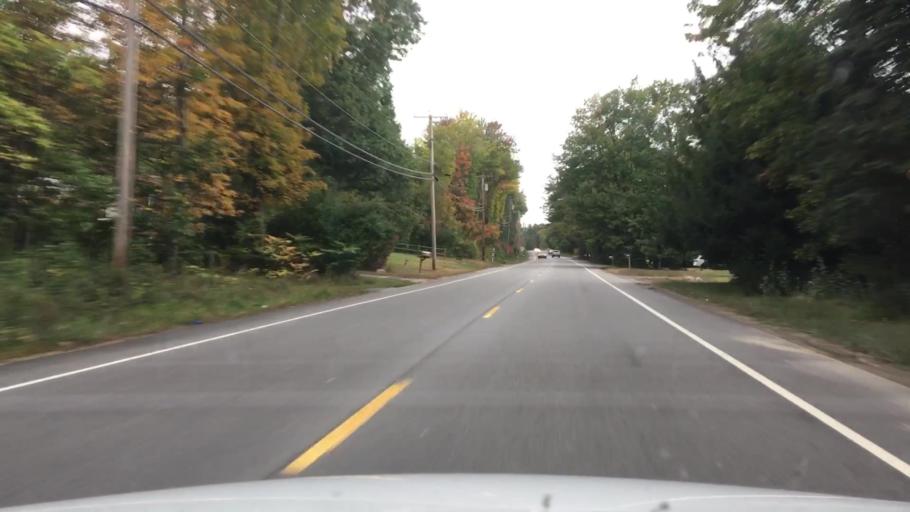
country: US
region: Maine
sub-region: Cumberland County
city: New Gloucester
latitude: 43.9110
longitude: -70.3512
